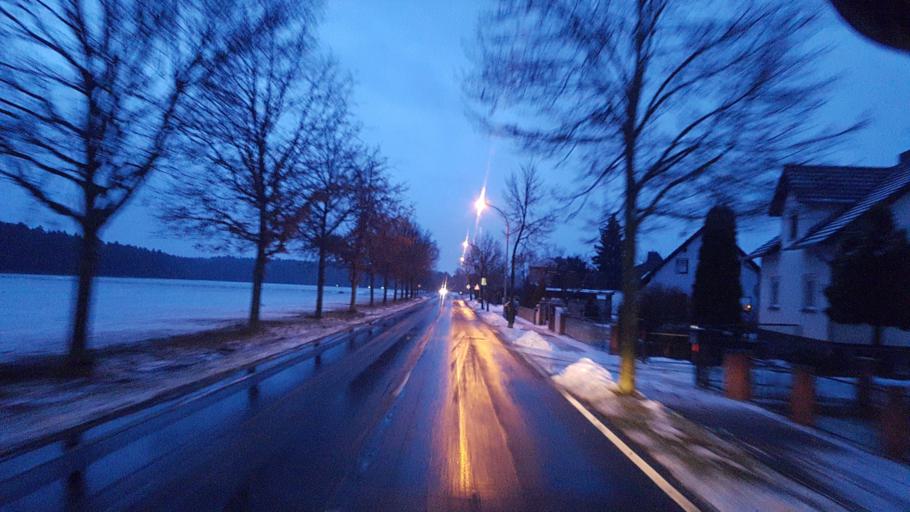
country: DE
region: Brandenburg
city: Briesen
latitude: 51.8098
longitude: 14.2467
